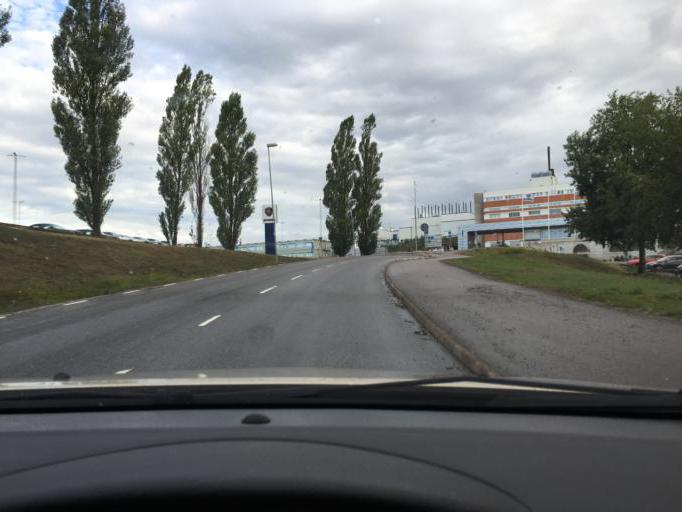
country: SE
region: Stockholm
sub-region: Sodertalje Kommun
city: Pershagen
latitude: 59.1657
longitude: 17.6362
